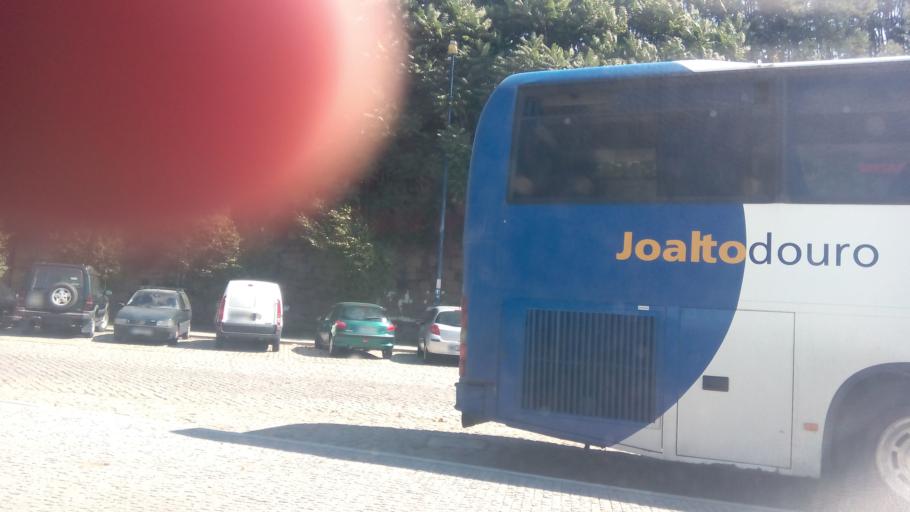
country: PT
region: Porto
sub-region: Penafiel
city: Penafiel
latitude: 41.2021
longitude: -8.2896
